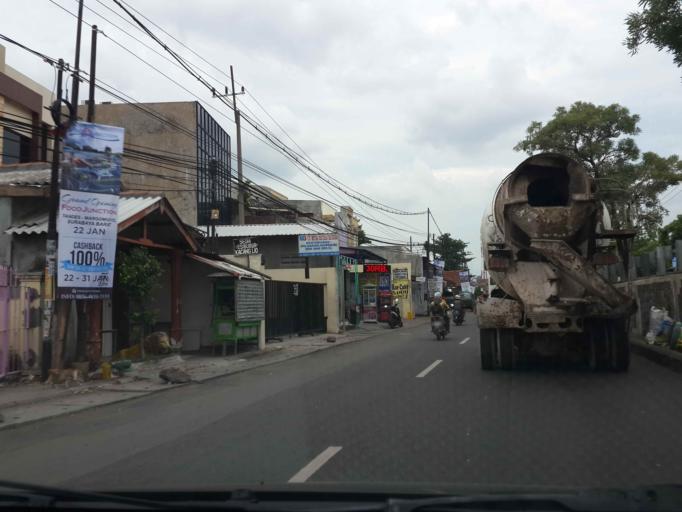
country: ID
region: East Java
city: Gubengairlangga
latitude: -7.2708
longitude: 112.7221
